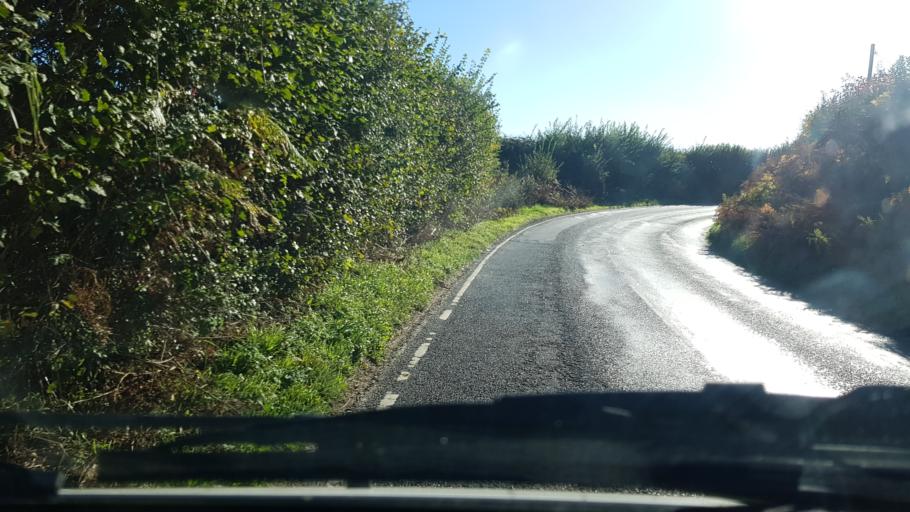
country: GB
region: England
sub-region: Surrey
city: Cranleigh
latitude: 51.1564
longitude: -0.4905
